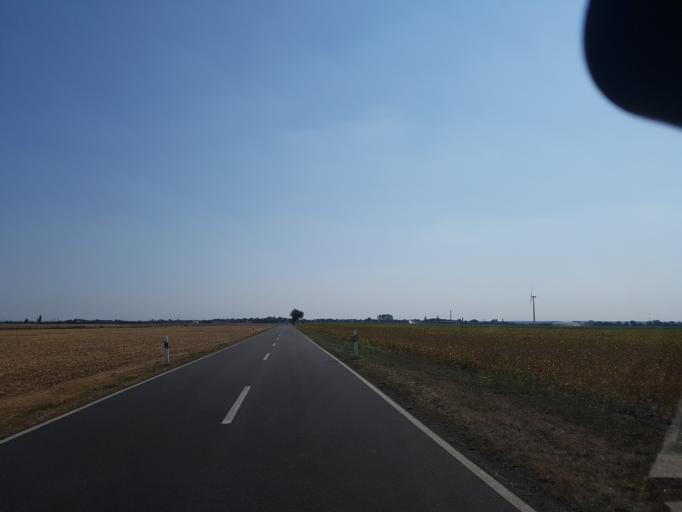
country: DE
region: Saxony-Anhalt
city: Prettin
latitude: 51.6632
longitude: 12.9907
